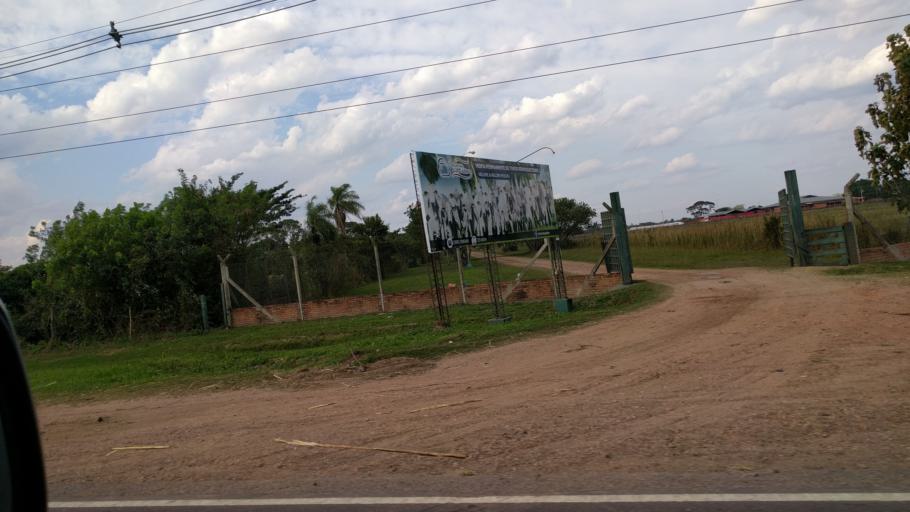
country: BO
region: Santa Cruz
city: Warnes
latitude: -17.5525
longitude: -63.1598
